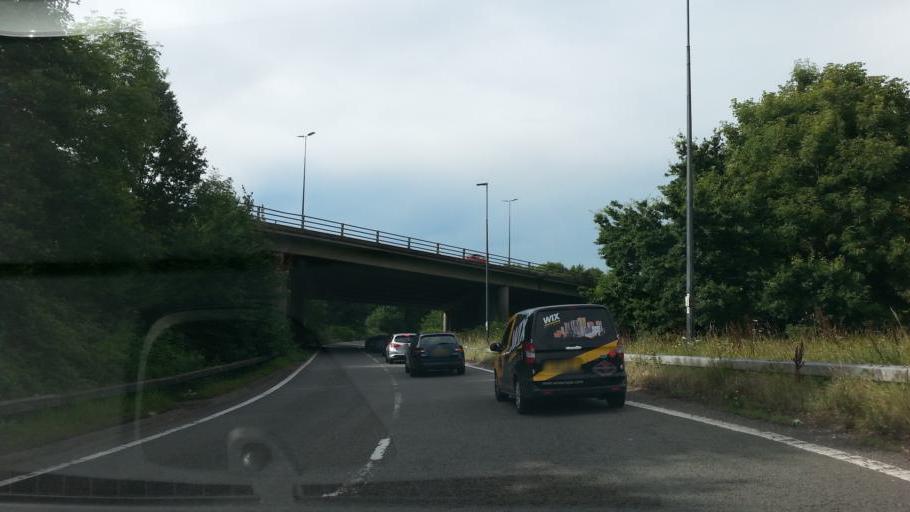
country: GB
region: Wales
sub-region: Newport
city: Newport
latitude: 51.5673
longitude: -3.0346
